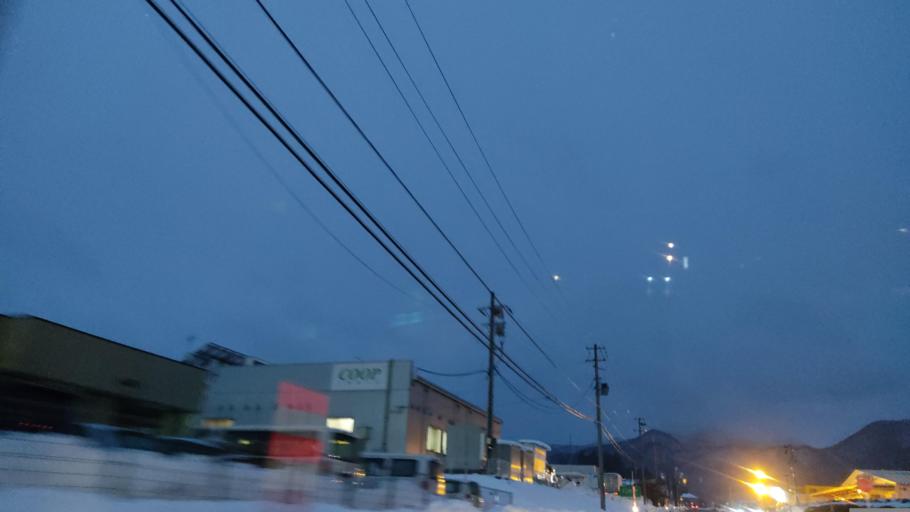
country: JP
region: Iwate
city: Morioka-shi
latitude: 39.6293
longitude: 141.1140
